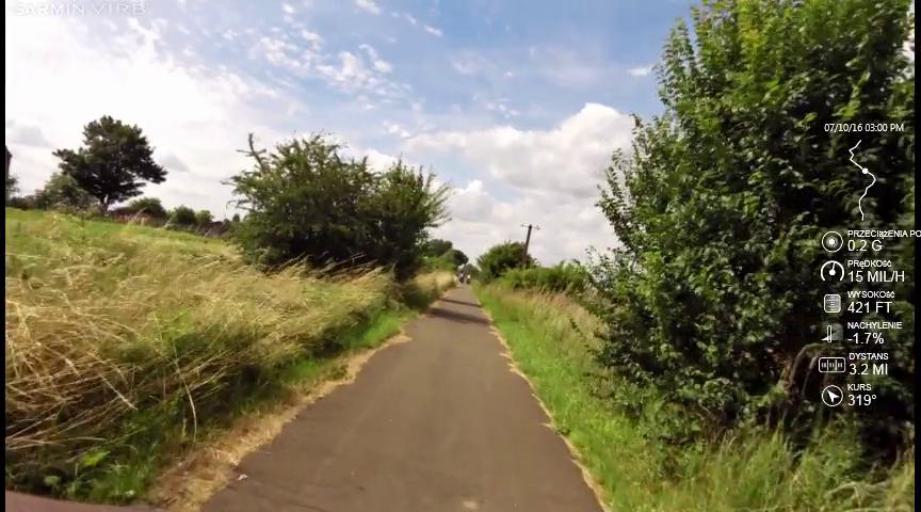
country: PL
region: West Pomeranian Voivodeship
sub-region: Powiat gryfinski
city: Banie
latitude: 53.1099
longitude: 14.6353
